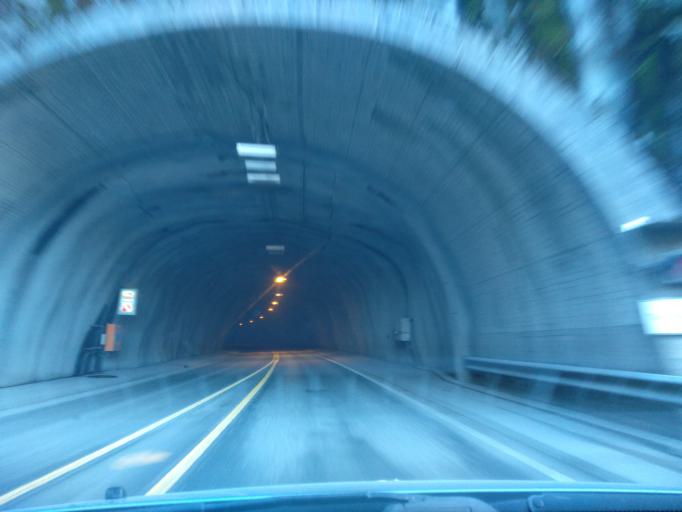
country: NO
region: Rogaland
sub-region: Sauda
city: Sauda
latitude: 59.8276
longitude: 6.2460
